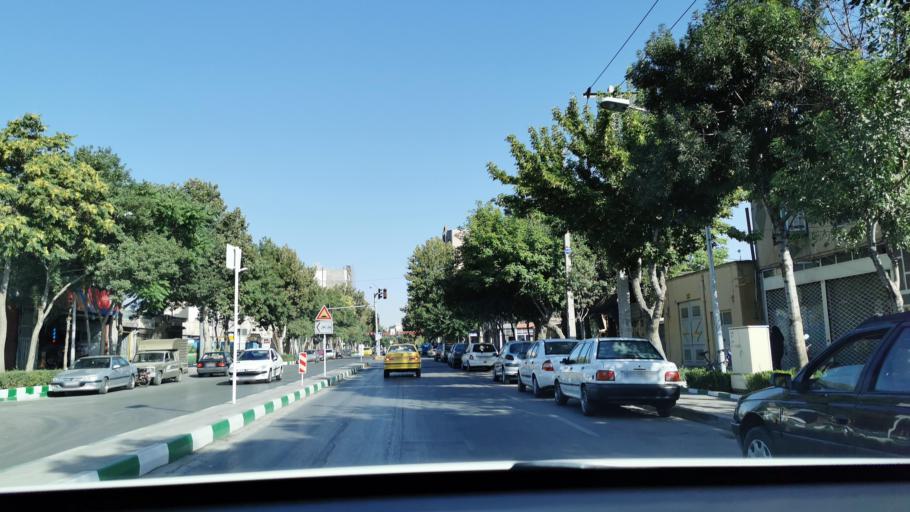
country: IR
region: Razavi Khorasan
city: Mashhad
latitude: 36.2982
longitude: 59.6203
